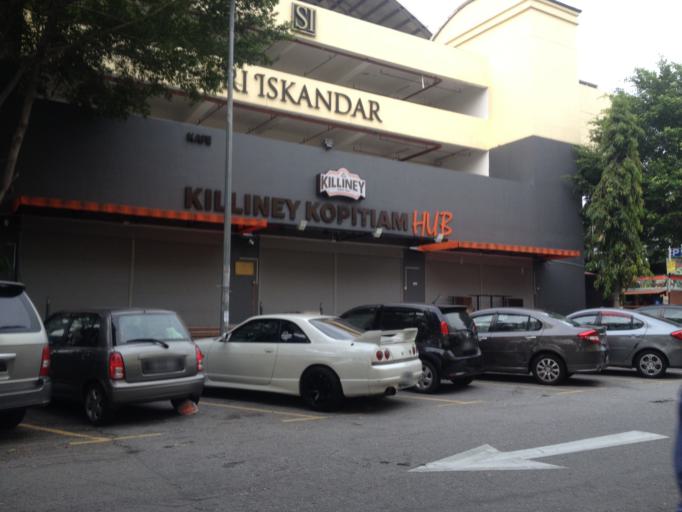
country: MY
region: Kuala Lumpur
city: Kuala Lumpur
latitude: 3.1790
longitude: 101.7415
